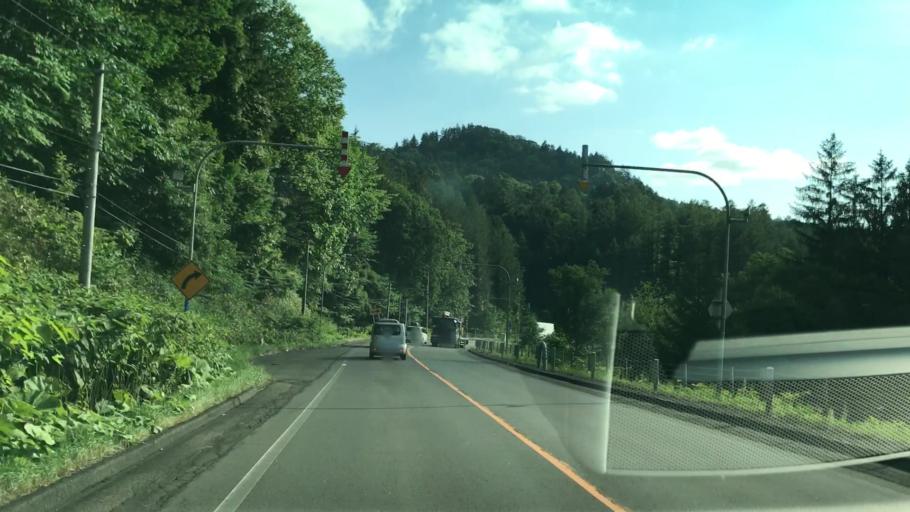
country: JP
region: Hokkaido
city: Iwamizawa
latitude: 42.9298
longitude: 142.1077
